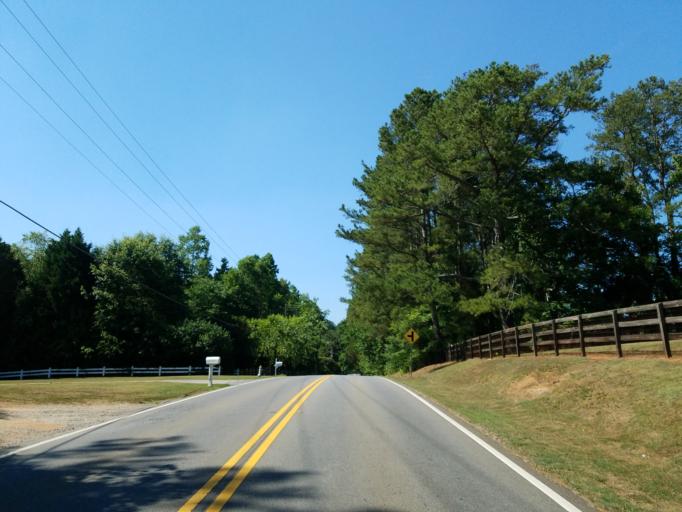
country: US
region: Georgia
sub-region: Fulton County
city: Milton
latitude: 34.1497
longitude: -84.3430
